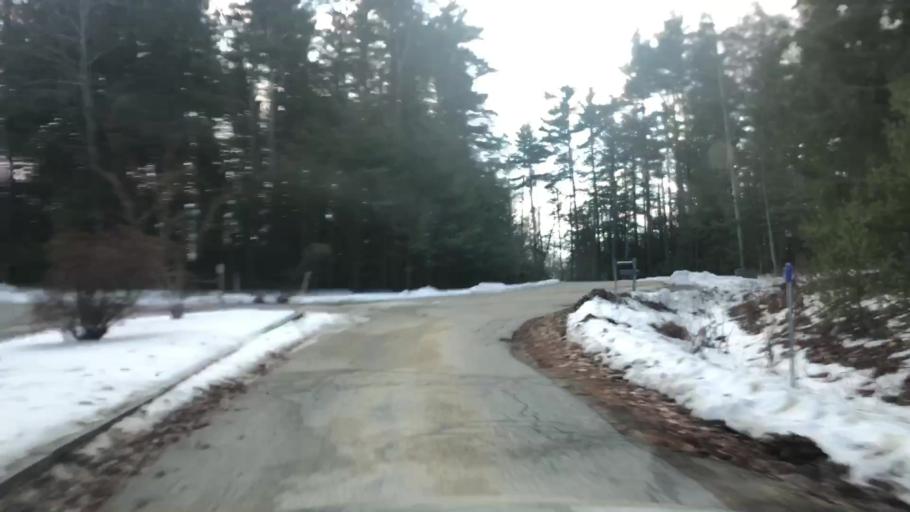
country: US
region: New Hampshire
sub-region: Hillsborough County
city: Milford
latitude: 42.8477
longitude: -71.6209
